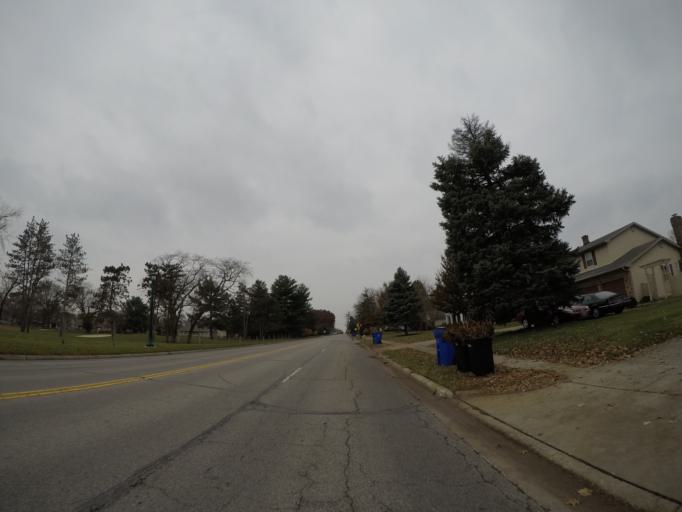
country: US
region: Ohio
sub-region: Franklin County
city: Upper Arlington
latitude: 40.0405
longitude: -83.0611
